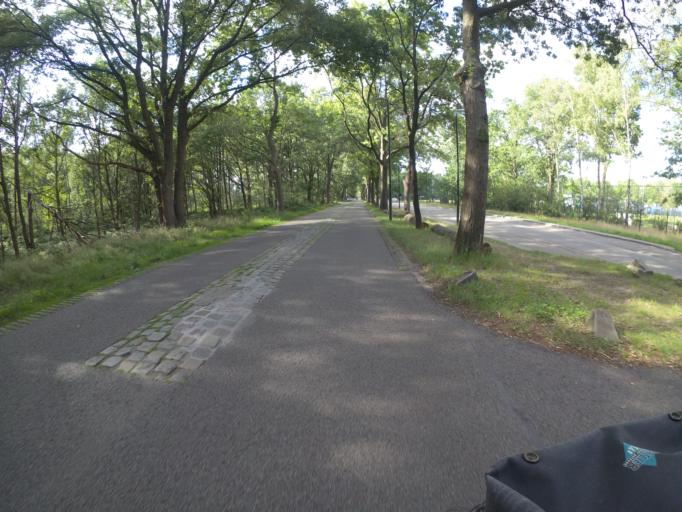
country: NL
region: North Brabant
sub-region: Gemeente Eindhoven
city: Eindhoven
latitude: 51.4112
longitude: 5.4714
